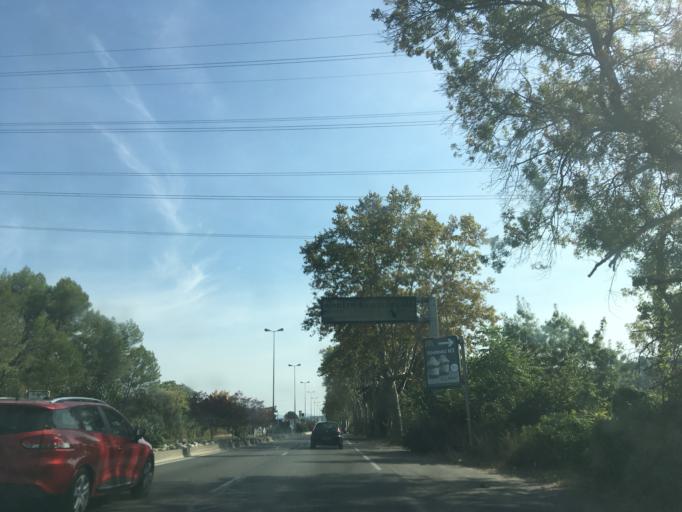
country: FR
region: Provence-Alpes-Cote d'Azur
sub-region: Departement du Var
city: Trans-en-Provence
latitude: 43.5127
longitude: 6.4781
